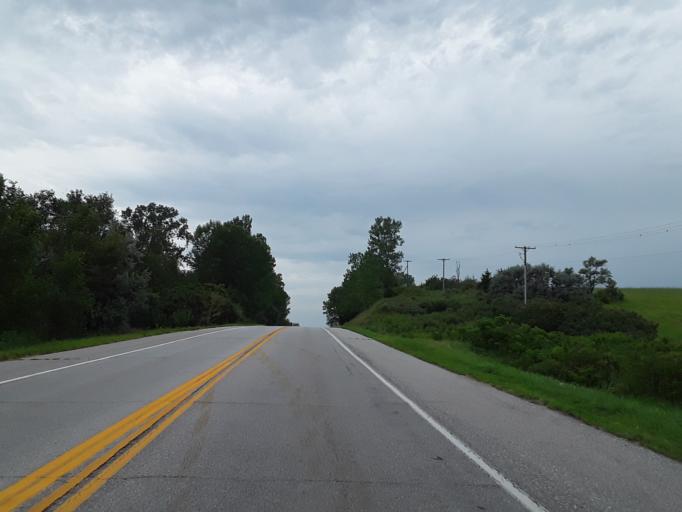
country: US
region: Nebraska
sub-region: Douglas County
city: Bennington
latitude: 41.3647
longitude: -96.0327
